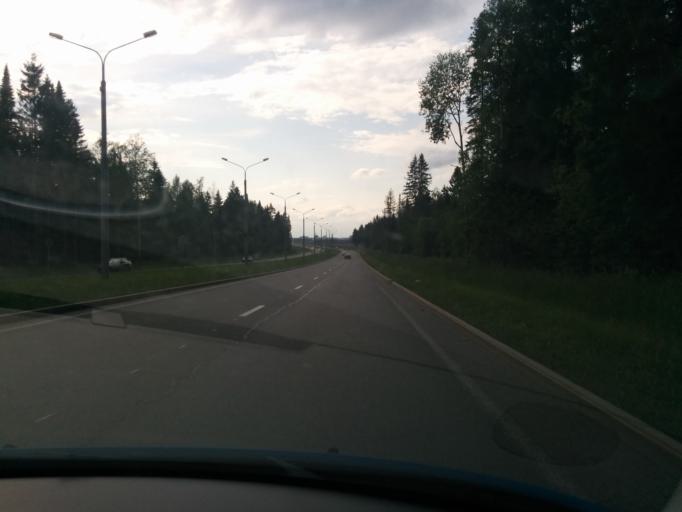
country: RU
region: Perm
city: Ferma
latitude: 58.0015
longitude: 56.3769
